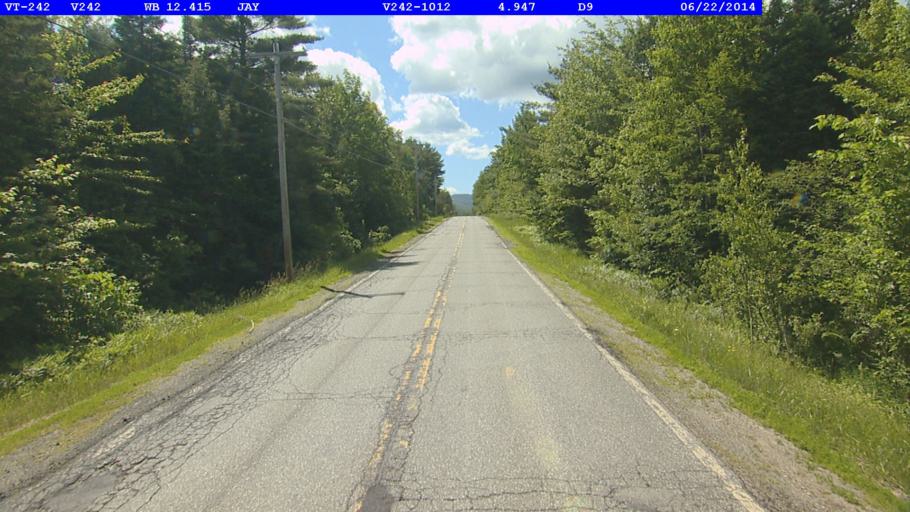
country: US
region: Vermont
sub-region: Orleans County
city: Newport
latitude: 44.9476
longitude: -72.4207
